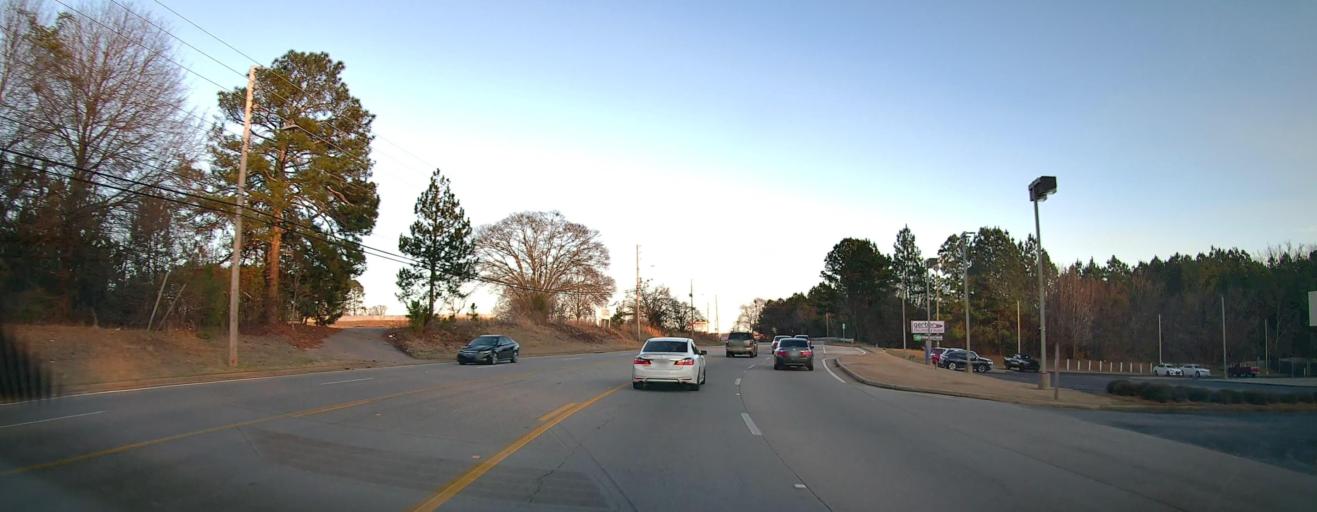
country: US
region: Georgia
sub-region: Troup County
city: La Grange
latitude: 33.0491
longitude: -85.0181
